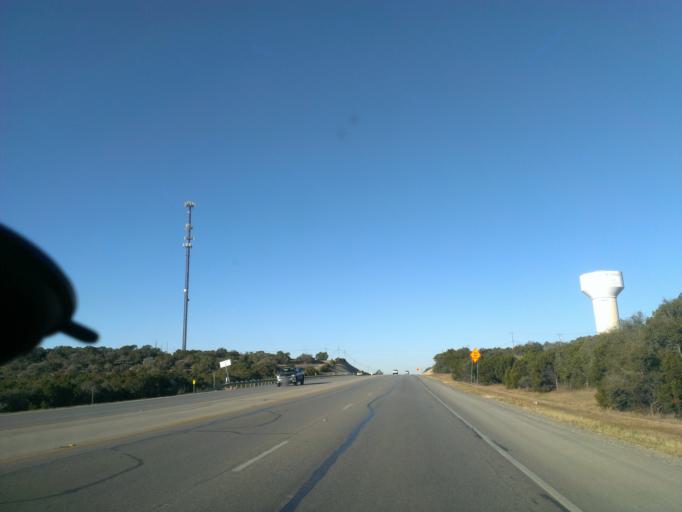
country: US
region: Texas
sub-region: Hays County
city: Dripping Springs
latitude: 30.1923
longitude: -98.0687
